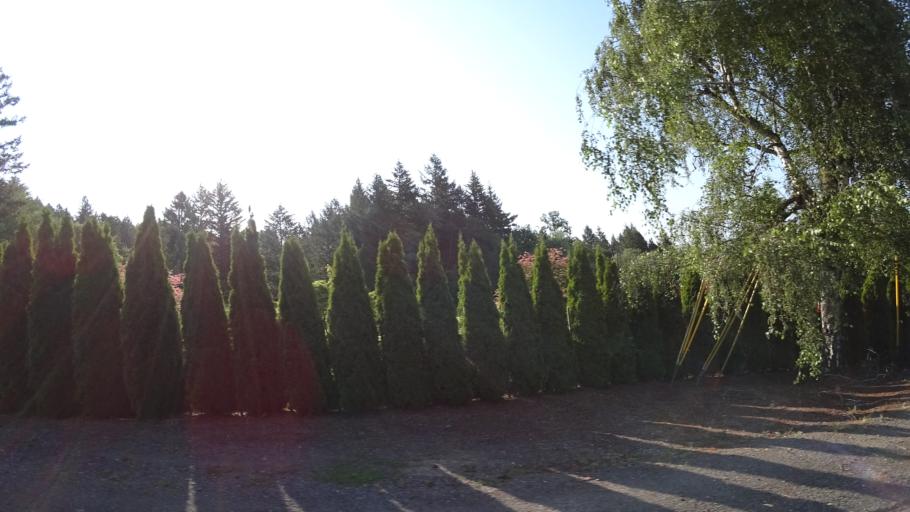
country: US
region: Oregon
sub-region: Washington County
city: Oak Hills
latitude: 45.5850
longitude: -122.8275
